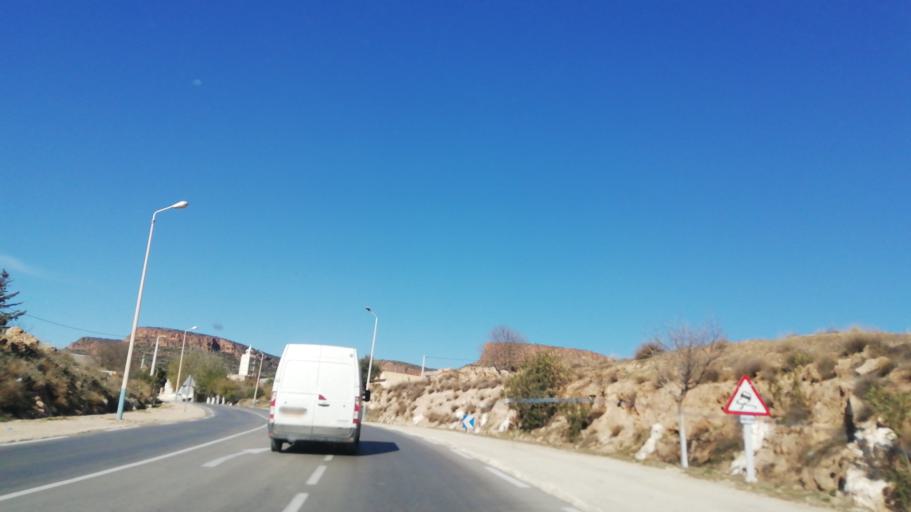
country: DZ
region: Tlemcen
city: Sebdou
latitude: 34.6789
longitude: -1.3140
